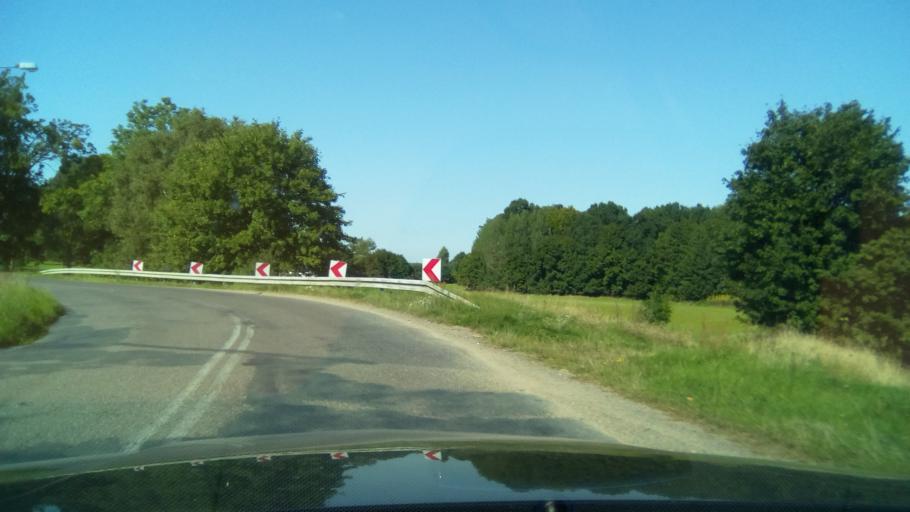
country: PL
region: West Pomeranian Voivodeship
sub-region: Powiat szczecinecki
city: Barwice
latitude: 53.7453
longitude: 16.3387
